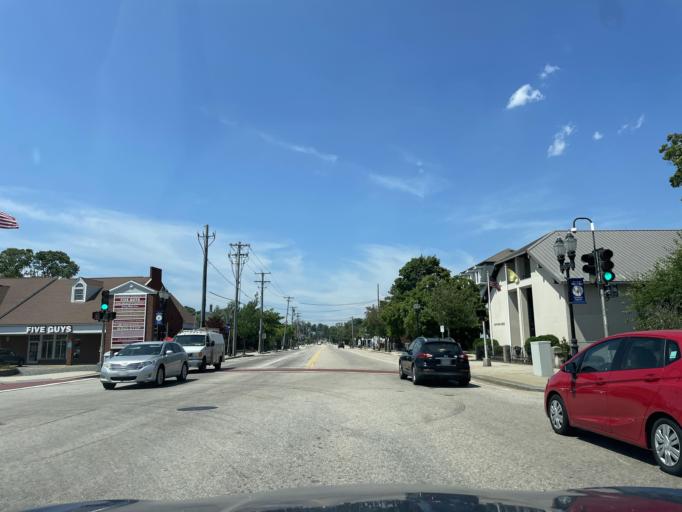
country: US
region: Massachusetts
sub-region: Norfolk County
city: Randolph
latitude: 42.1656
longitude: -71.0433
